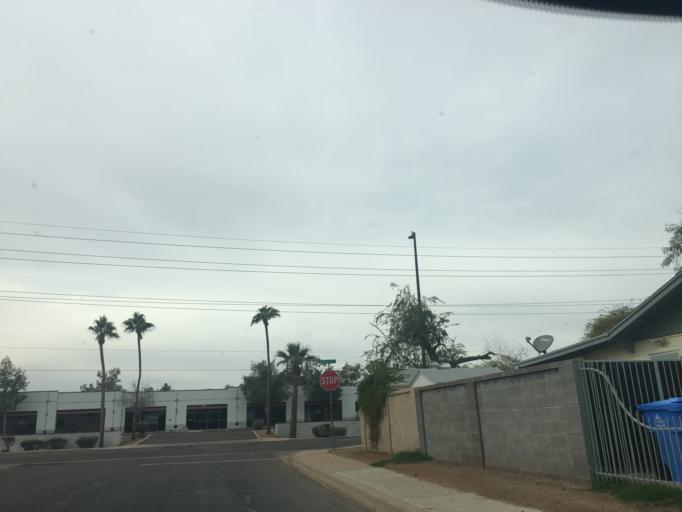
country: US
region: Arizona
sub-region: Maricopa County
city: Gilbert
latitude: 33.3621
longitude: -111.7980
